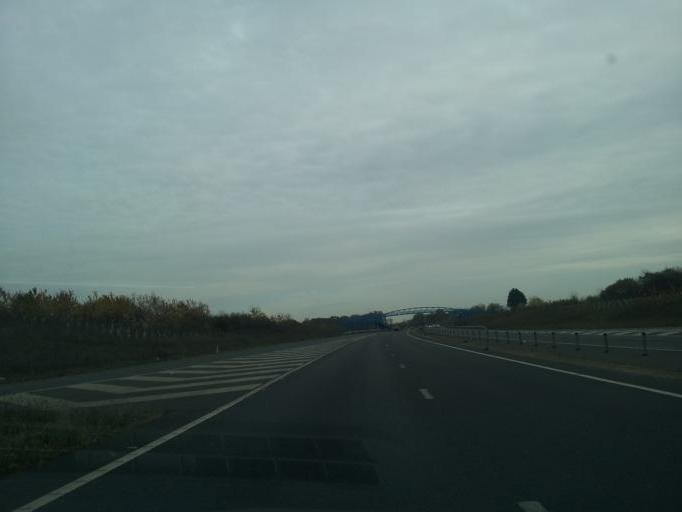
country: GB
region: England
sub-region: Cambridgeshire
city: Comberton
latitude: 52.2198
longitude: 0.0047
